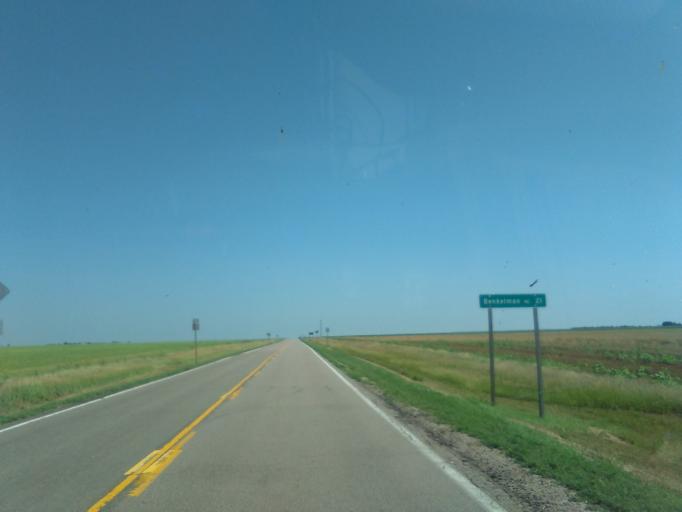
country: US
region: Kansas
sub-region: Cheyenne County
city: Saint Francis
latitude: 39.7584
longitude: -101.5421
